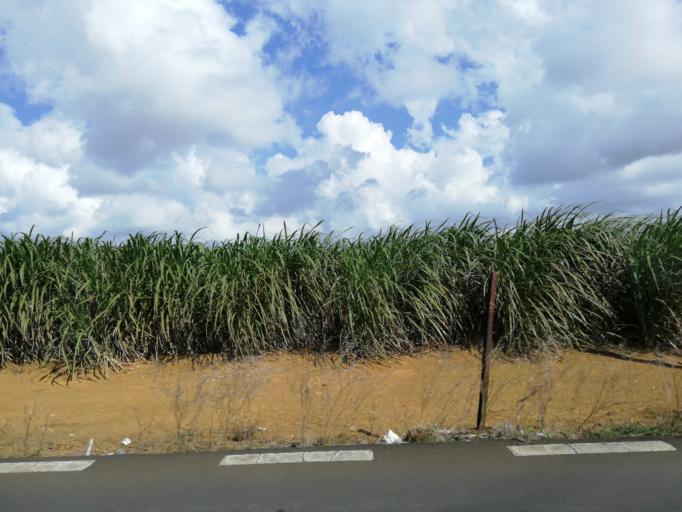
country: MU
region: Pamplemousses
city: Creve Coeur
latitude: -20.2106
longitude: 57.5622
